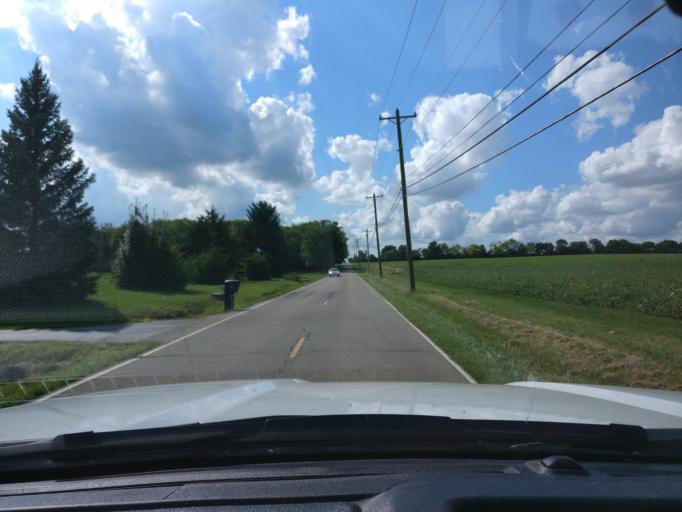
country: US
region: Ohio
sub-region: Warren County
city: Springboro
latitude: 39.5069
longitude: -84.2332
